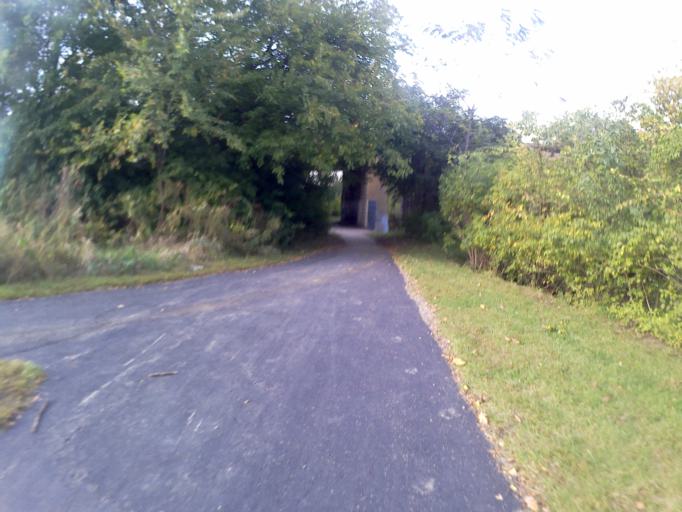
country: US
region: Illinois
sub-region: DuPage County
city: Lisle
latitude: 41.7962
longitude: -88.0803
